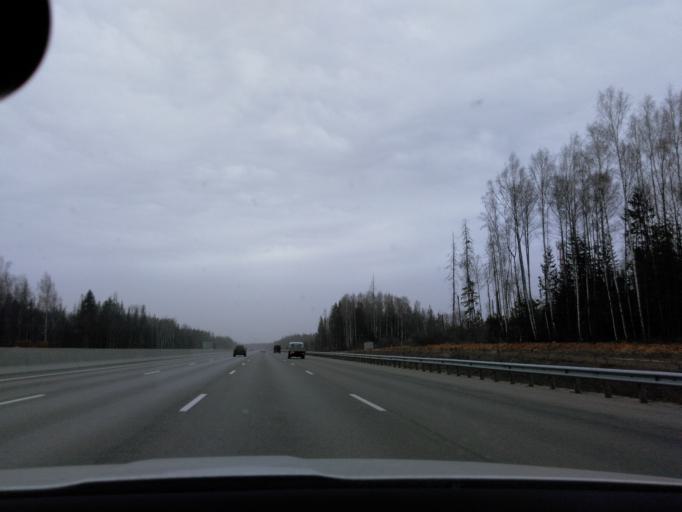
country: RU
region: Moskovskaya
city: Rzhavki
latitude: 56.0027
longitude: 37.2928
